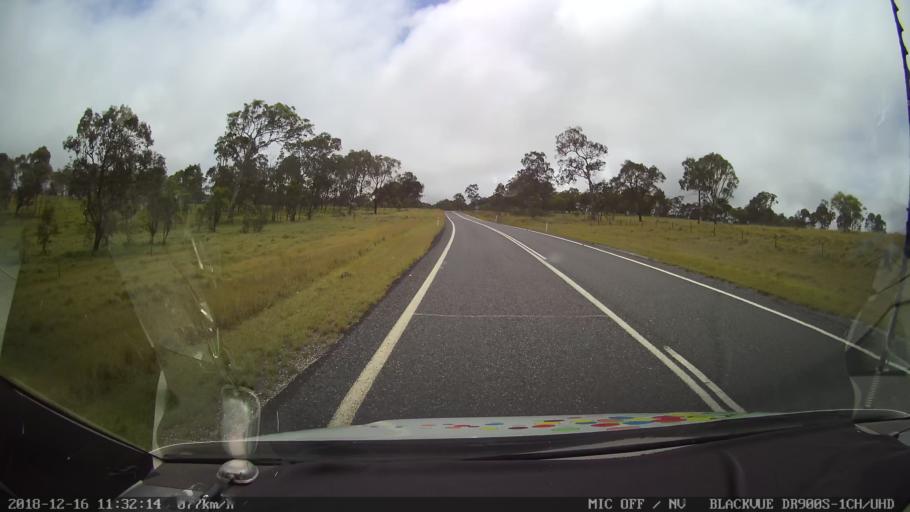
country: AU
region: New South Wales
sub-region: Tenterfield Municipality
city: Carrolls Creek
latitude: -29.0151
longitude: 152.1326
